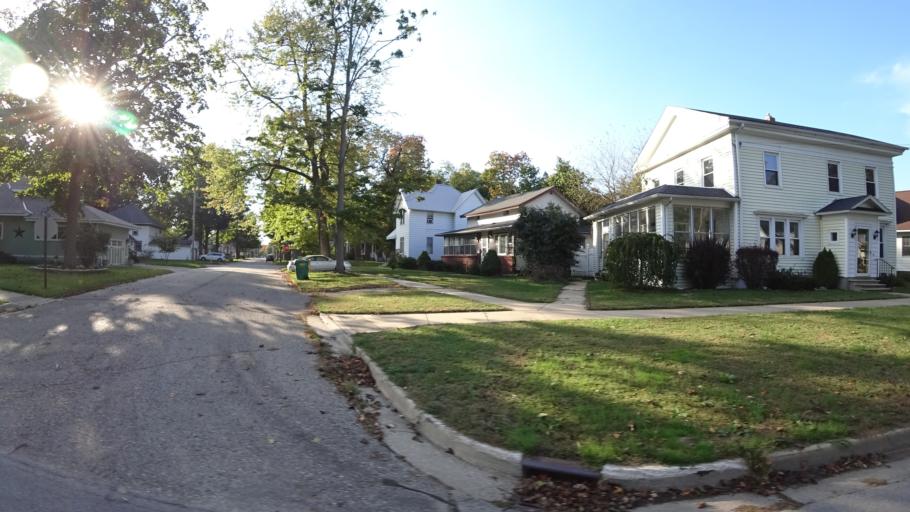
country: US
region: Michigan
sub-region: Saint Joseph County
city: Three Rivers
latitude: 41.9499
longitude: -85.6314
